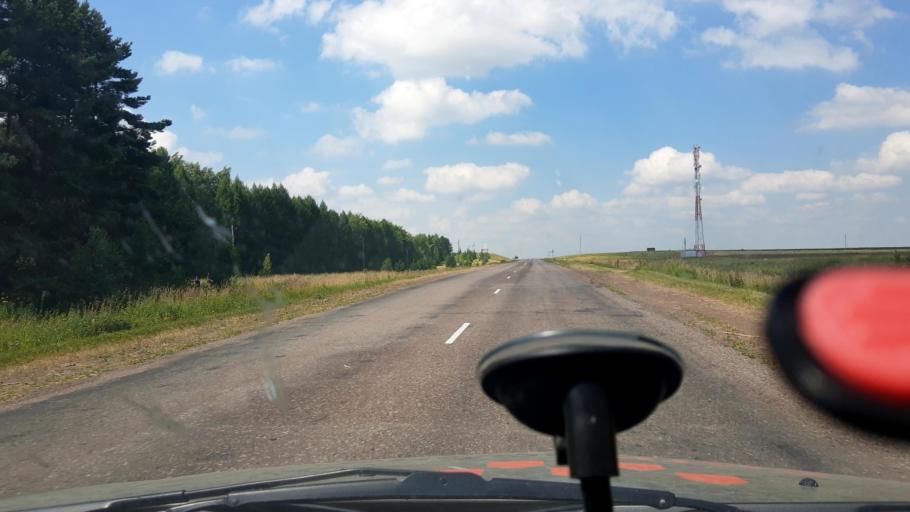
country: RU
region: Bashkortostan
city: Chekmagush
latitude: 54.9429
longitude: 54.5654
